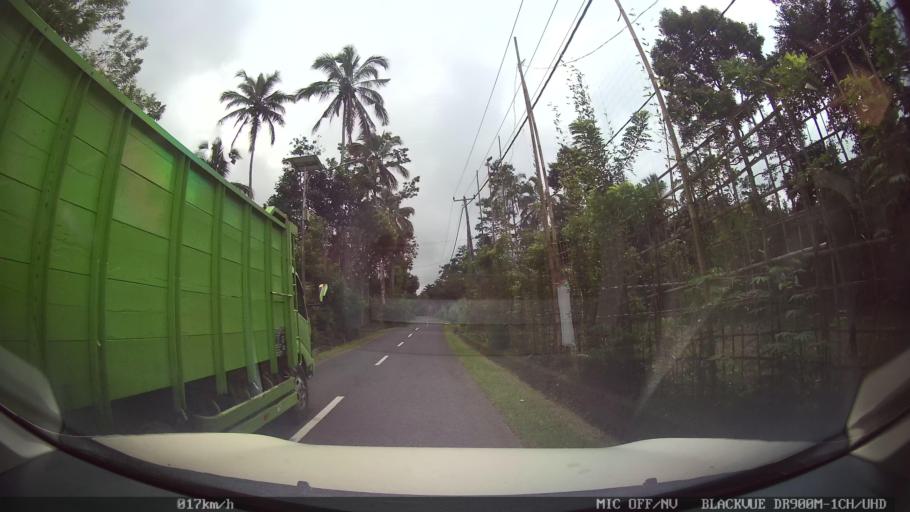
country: ID
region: Bali
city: Banjar Geriana Kangin
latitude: -8.3970
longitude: 115.4414
